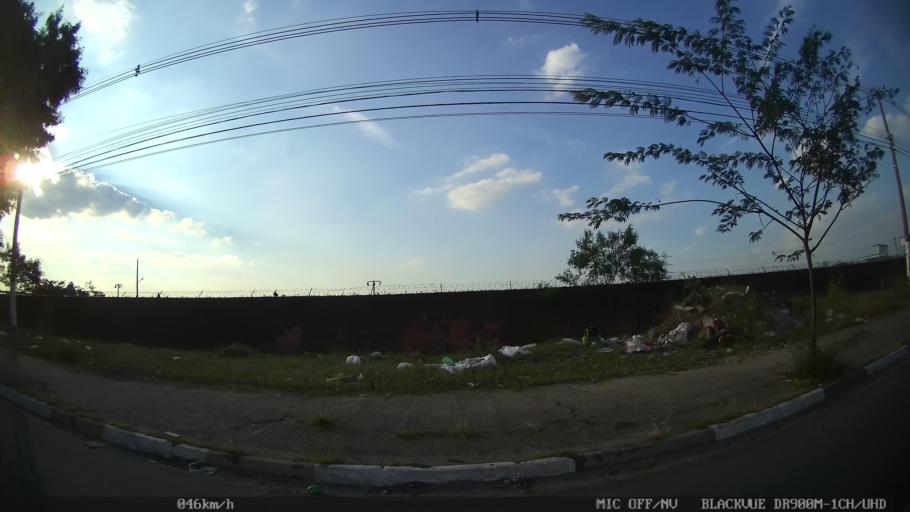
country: BR
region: Sao Paulo
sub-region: Hortolandia
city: Hortolandia
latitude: -22.8583
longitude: -47.1667
